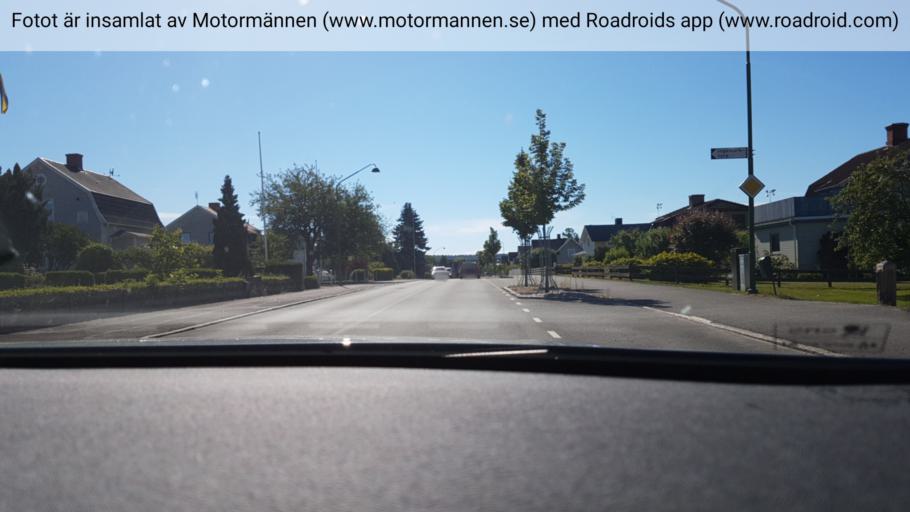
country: SE
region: Vaestra Goetaland
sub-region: Tidaholms Kommun
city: Tidaholm
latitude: 58.1883
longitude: 13.9508
